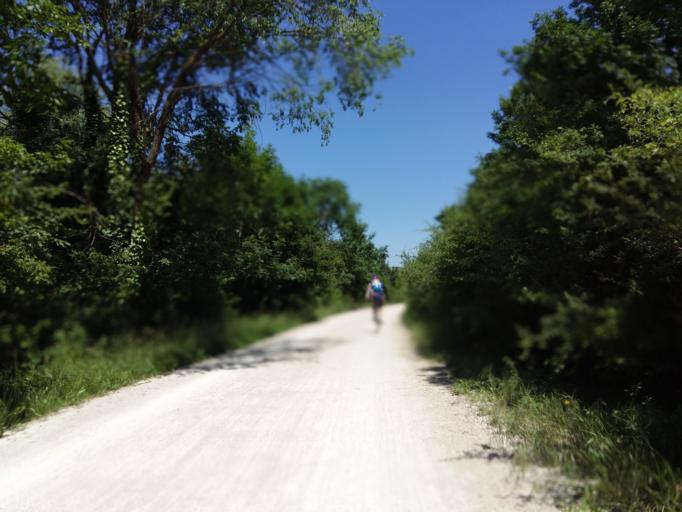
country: FR
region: Rhone-Alpes
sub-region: Departement du Rhone
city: Caluire-et-Cuire
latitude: 45.7829
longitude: 4.8476
